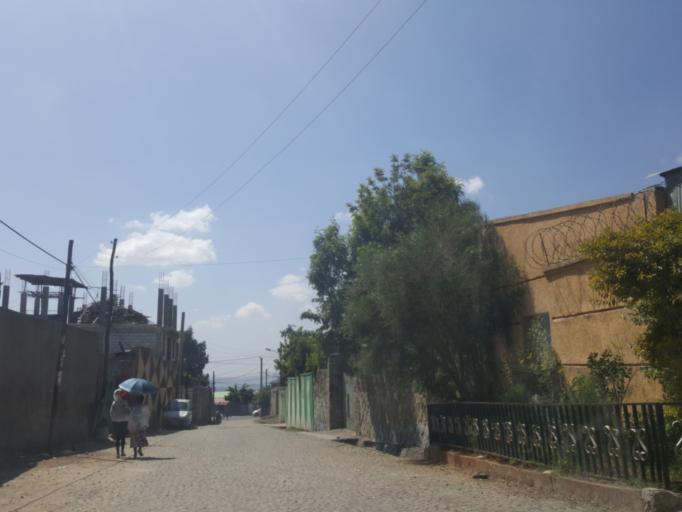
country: ET
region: Adis Abeba
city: Addis Ababa
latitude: 9.0583
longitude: 38.7300
